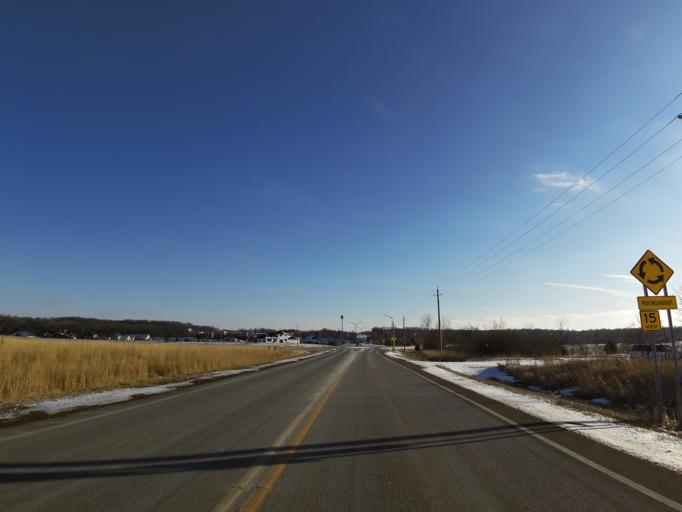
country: US
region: Minnesota
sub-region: Scott County
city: Prior Lake
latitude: 44.7650
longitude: -93.4494
